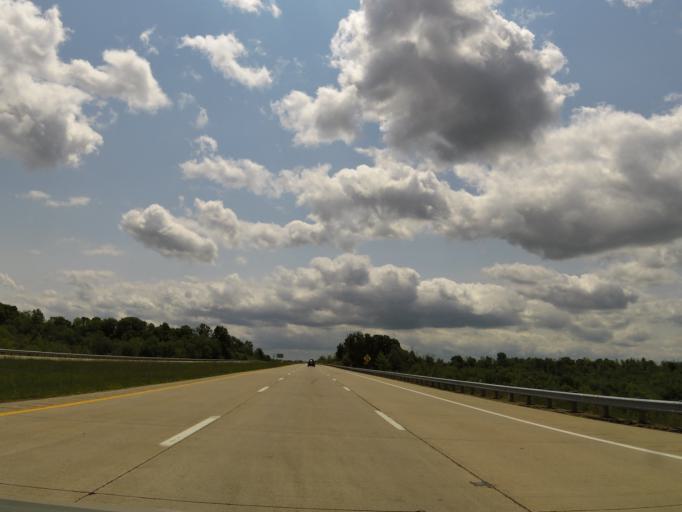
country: US
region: Ohio
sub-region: Athens County
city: Athens
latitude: 39.2861
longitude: -82.1014
